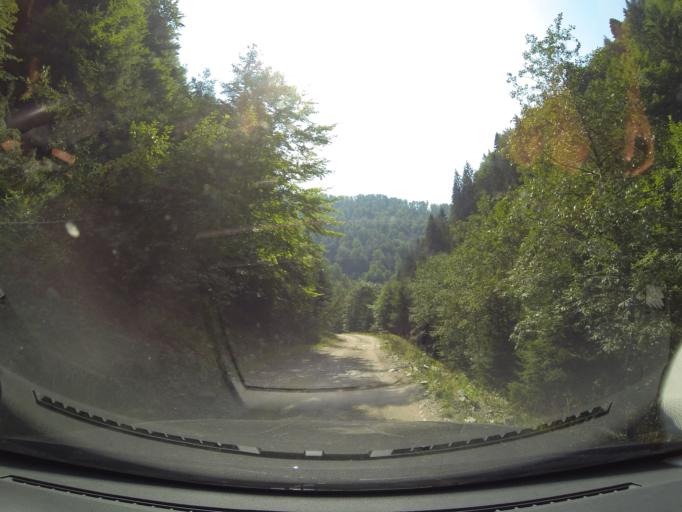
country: RO
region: Arges
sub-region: Comuna Arefu
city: Arefu
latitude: 45.5123
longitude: 24.6686
